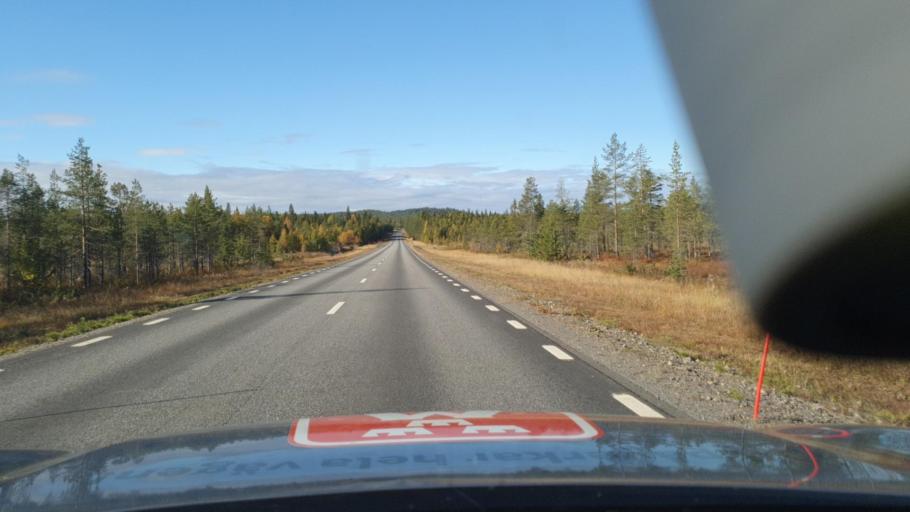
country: SE
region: Norrbotten
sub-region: Arvidsjaurs Kommun
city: Arvidsjaur
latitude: 65.6643
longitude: 19.8949
